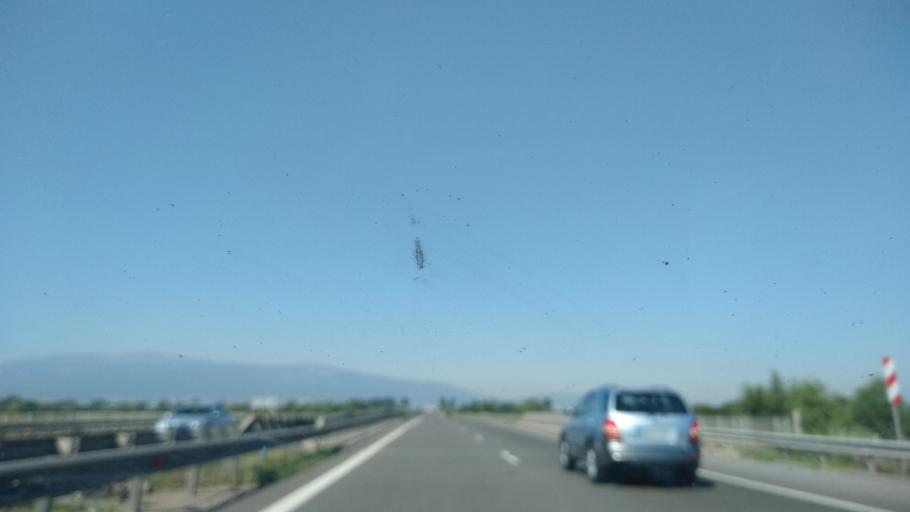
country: BG
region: Sofia-Capital
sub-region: Stolichna Obshtina
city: Bukhovo
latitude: 42.7161
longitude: 23.4815
